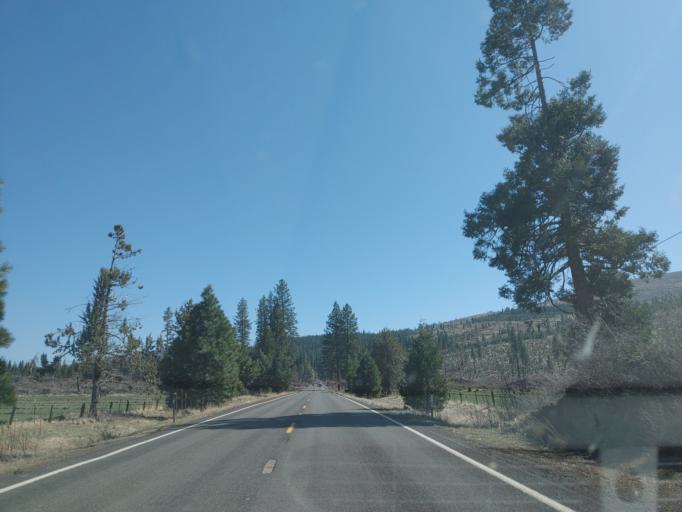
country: US
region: California
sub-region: Shasta County
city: Burney
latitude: 40.7679
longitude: -121.5006
